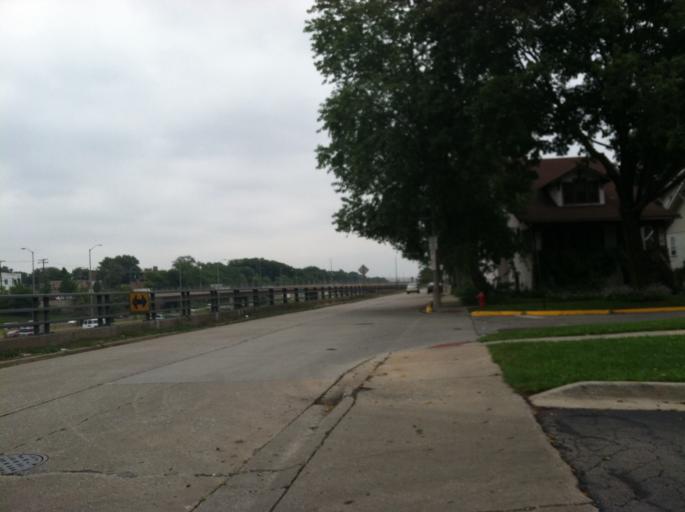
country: US
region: Illinois
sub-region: Cook County
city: Oak Park
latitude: 41.8714
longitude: -87.7869
